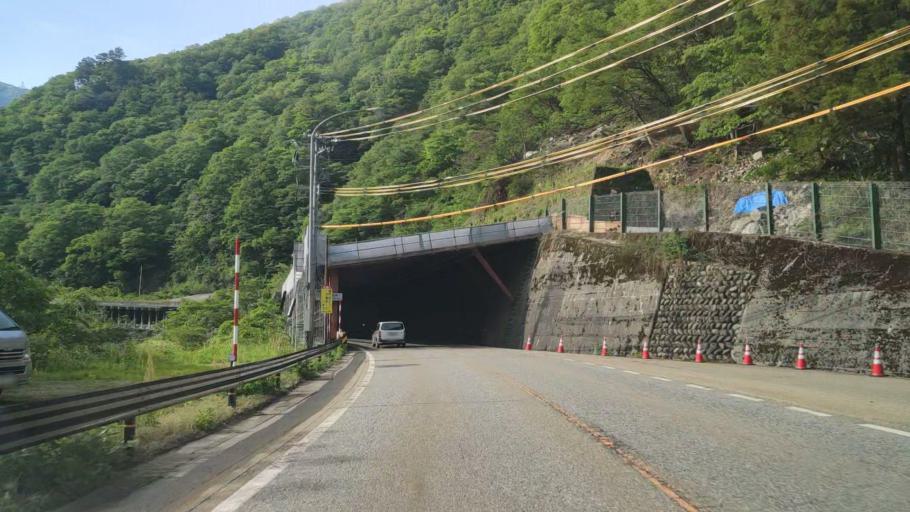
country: JP
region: Toyama
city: Yatsuomachi-higashikumisaka
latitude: 36.3805
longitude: 137.2801
